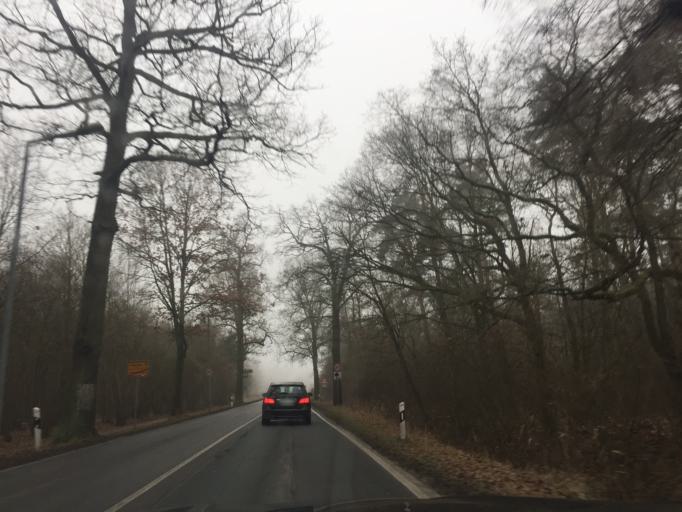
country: DE
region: Brandenburg
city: Falkensee
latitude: 52.5959
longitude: 13.1006
